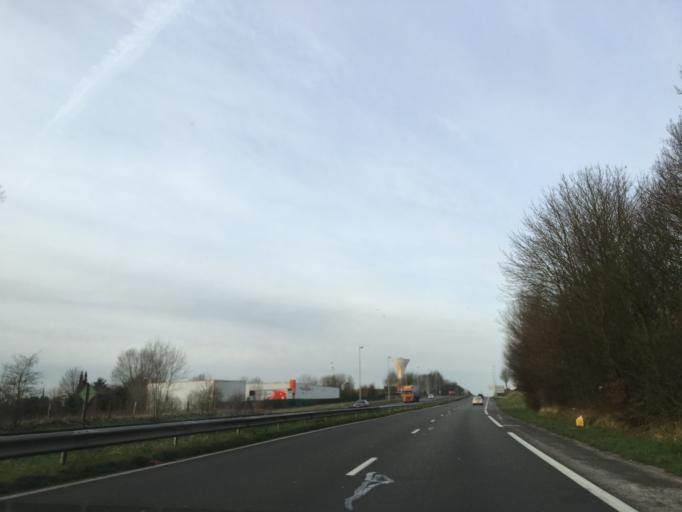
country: FR
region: Nord-Pas-de-Calais
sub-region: Departement du Pas-de-Calais
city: Saint-Laurent-Blangy
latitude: 50.3074
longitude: 2.8104
